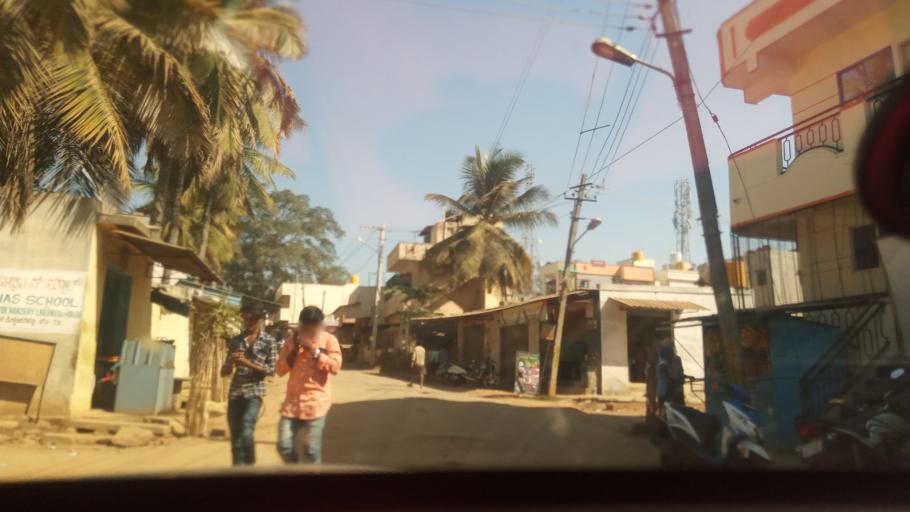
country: IN
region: Karnataka
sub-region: Bangalore Rural
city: Nelamangala
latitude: 13.0365
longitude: 77.4921
